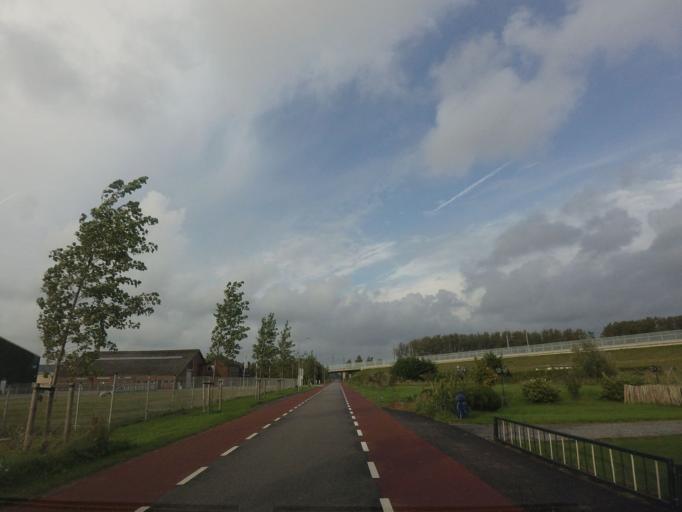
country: NL
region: South Holland
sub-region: Gemeente Kaag en Braassem
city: Oude Wetering
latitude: 52.2332
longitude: 4.6292
